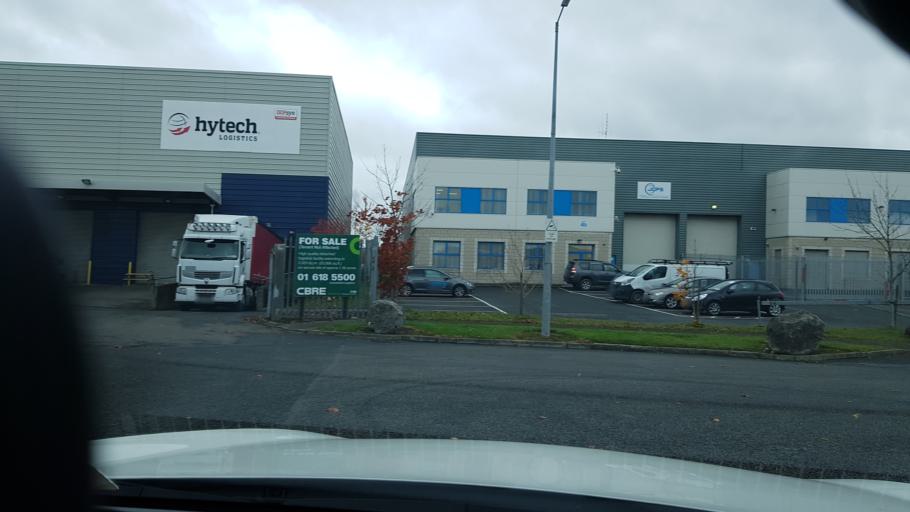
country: IE
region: Leinster
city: Castleknock
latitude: 53.4009
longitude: -6.3427
